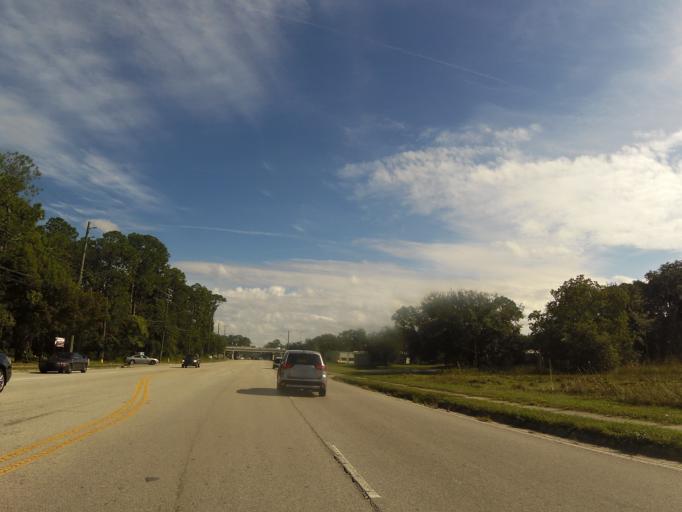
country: US
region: Florida
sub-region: Duval County
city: Jacksonville
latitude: 30.2648
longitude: -81.6121
